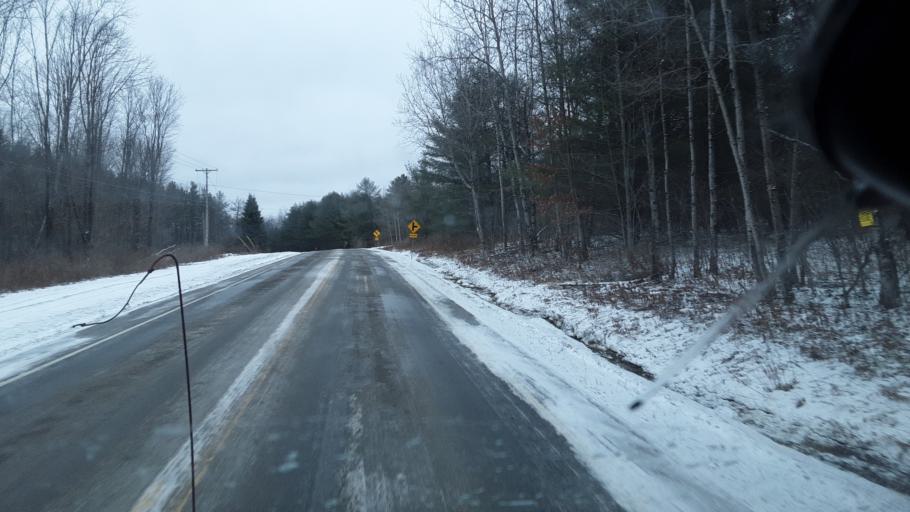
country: US
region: New York
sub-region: Allegany County
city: Friendship
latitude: 42.2259
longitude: -78.1406
